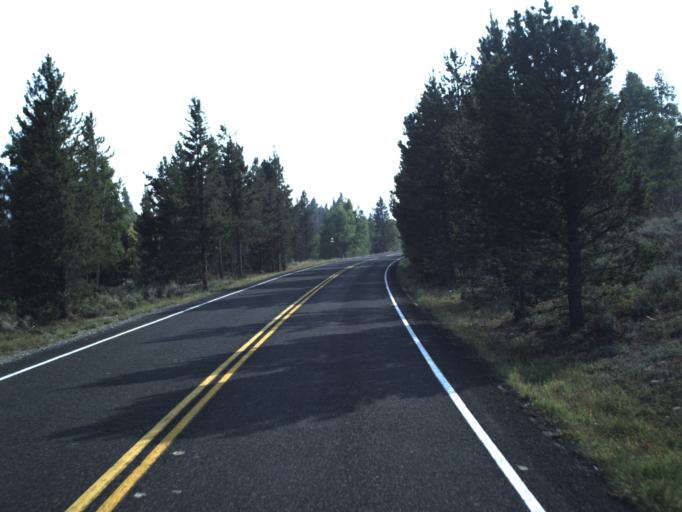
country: US
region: Wyoming
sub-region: Uinta County
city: Evanston
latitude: 40.8315
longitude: -110.8530
